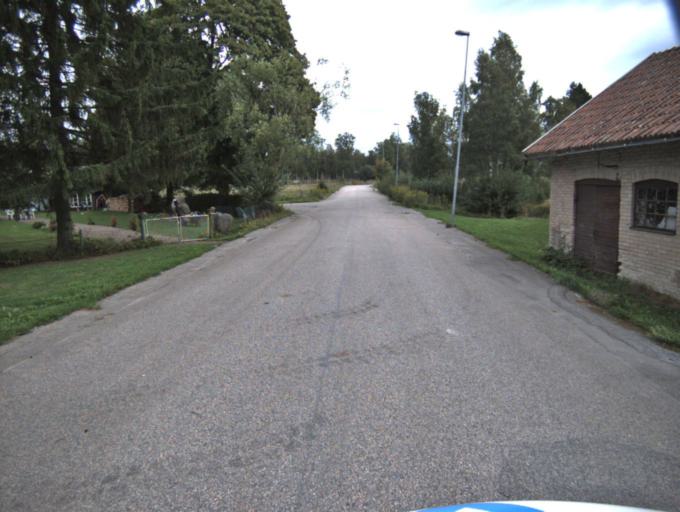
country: SE
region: Vaestra Goetaland
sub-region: Falkopings Kommun
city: Falkoeping
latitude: 57.9881
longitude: 13.5340
